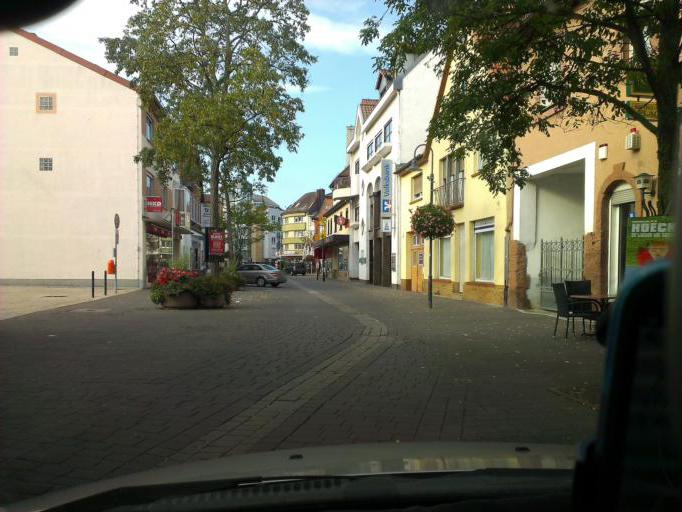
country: DE
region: Hesse
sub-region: Regierungsbezirk Darmstadt
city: Burstadt
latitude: 49.6418
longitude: 8.4559
